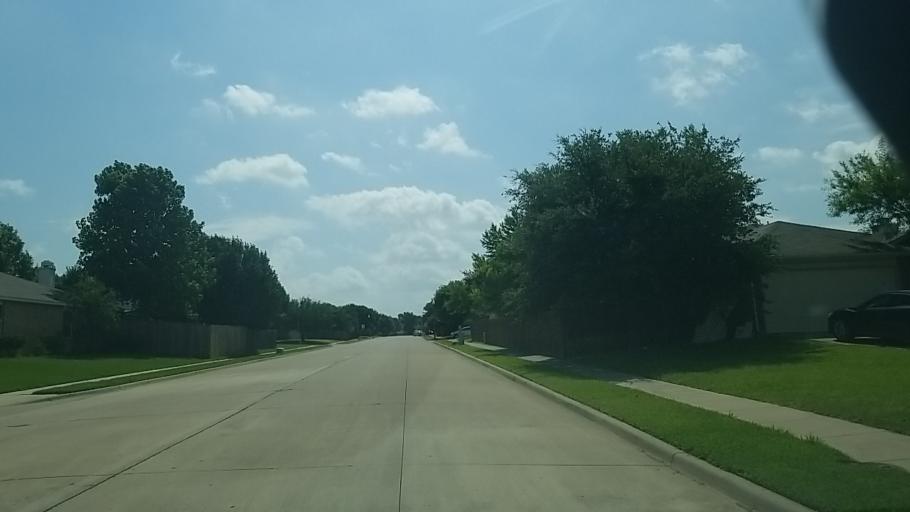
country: US
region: Texas
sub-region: Denton County
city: Copper Canyon
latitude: 33.1422
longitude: -97.1160
